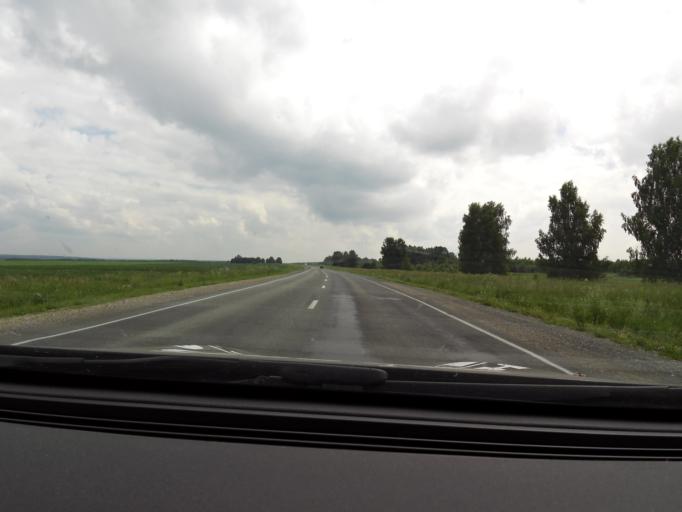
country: RU
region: Perm
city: Suksun
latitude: 56.9445
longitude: 57.5315
